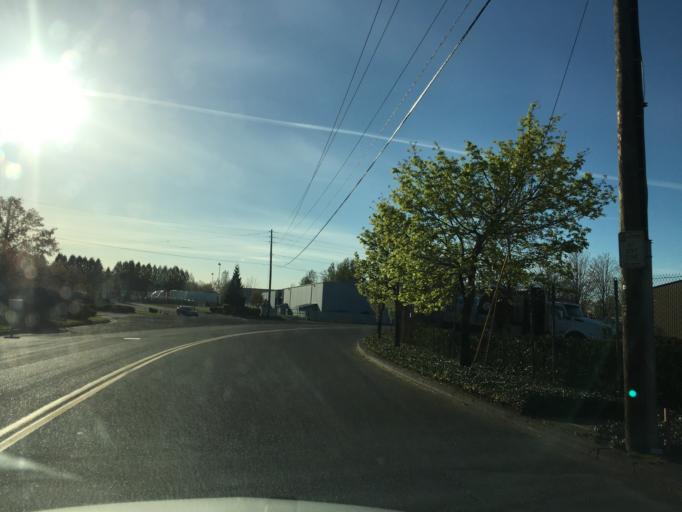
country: US
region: Oregon
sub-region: Multnomah County
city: Lents
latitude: 45.5582
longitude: -122.5278
